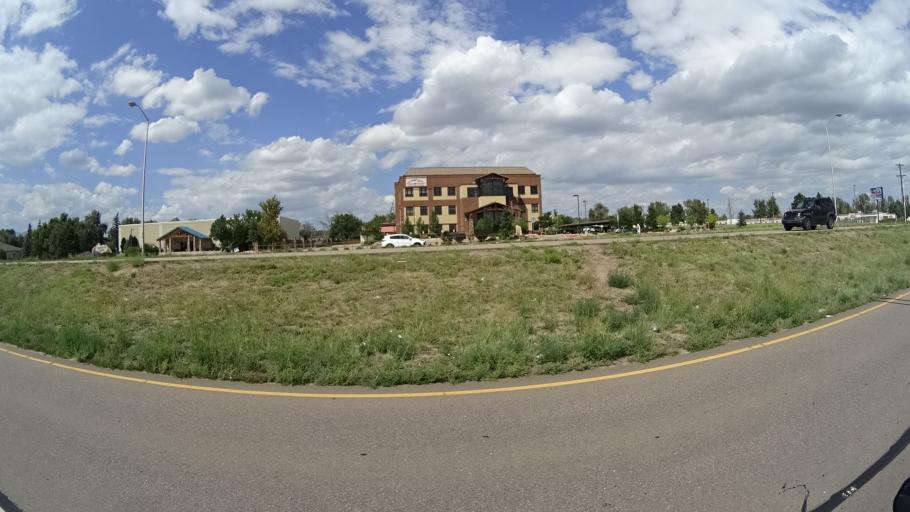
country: US
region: Colorado
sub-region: El Paso County
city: Cimarron Hills
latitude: 38.8393
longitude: -104.7325
